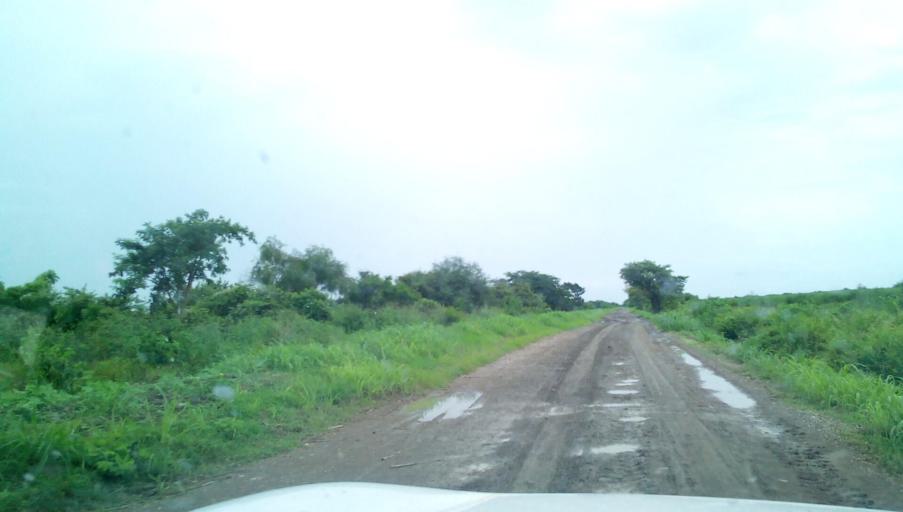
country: MX
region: Veracruz
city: Panuco
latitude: 21.8257
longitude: -98.1108
